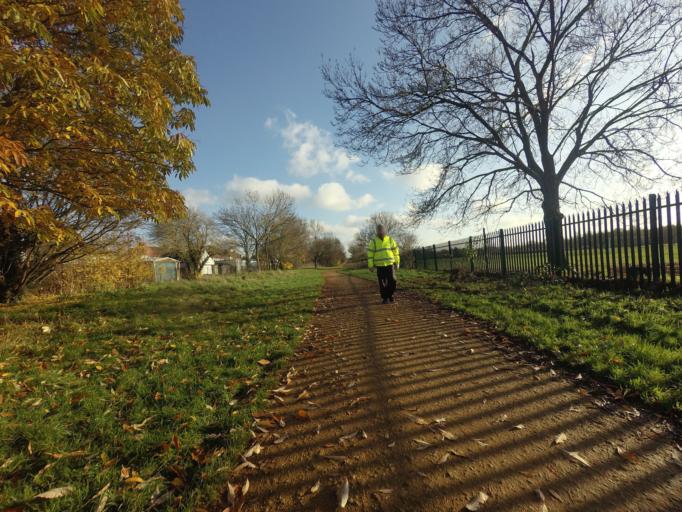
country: GB
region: England
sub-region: Greater London
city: Feltham
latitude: 51.4442
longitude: -0.3988
